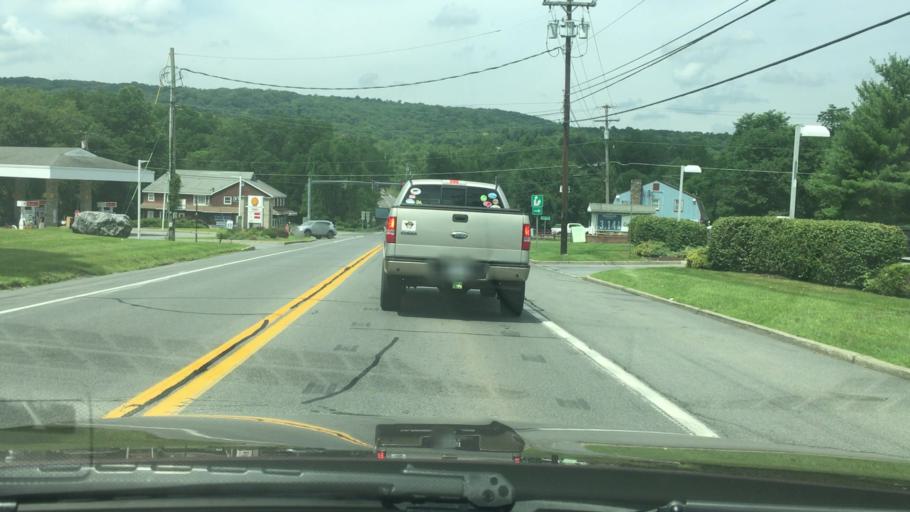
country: US
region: New York
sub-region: Dutchess County
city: Hillside Lake
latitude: 41.6287
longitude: -73.6956
